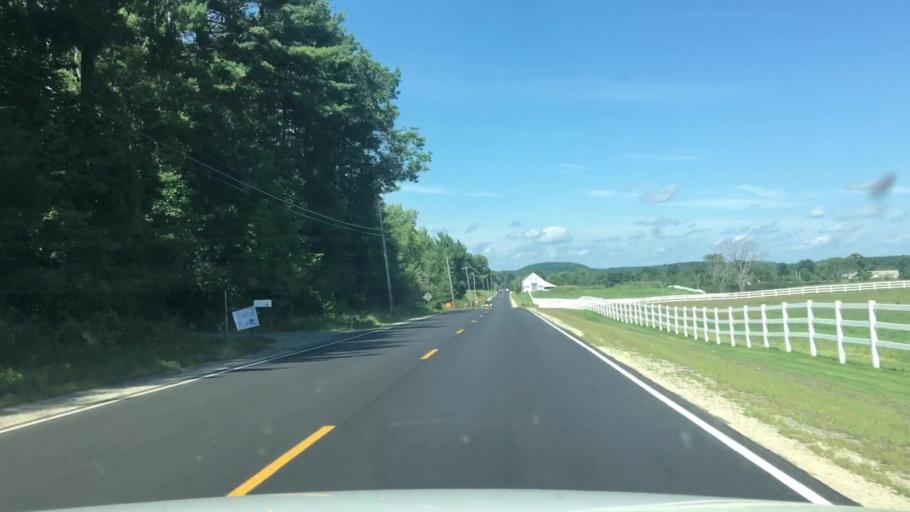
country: US
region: Maine
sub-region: Cumberland County
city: Cumberland Center
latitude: 43.7821
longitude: -70.3039
